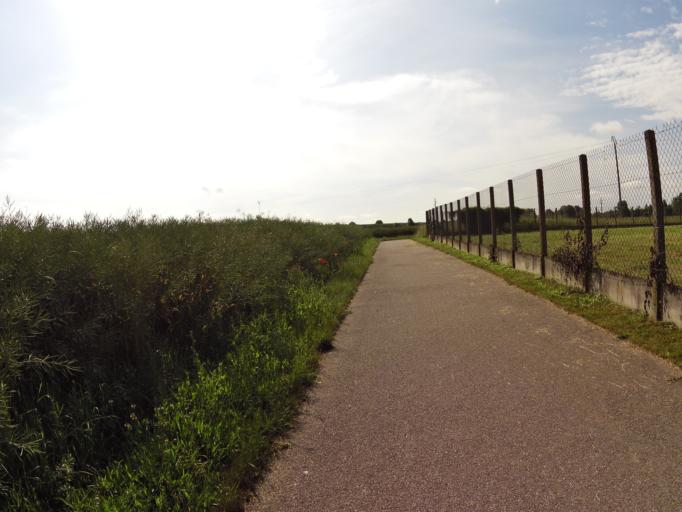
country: FR
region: Champagne-Ardenne
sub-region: Departement de l'Aube
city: Saint-Julien-les-Villas
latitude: 48.2666
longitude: 4.1110
